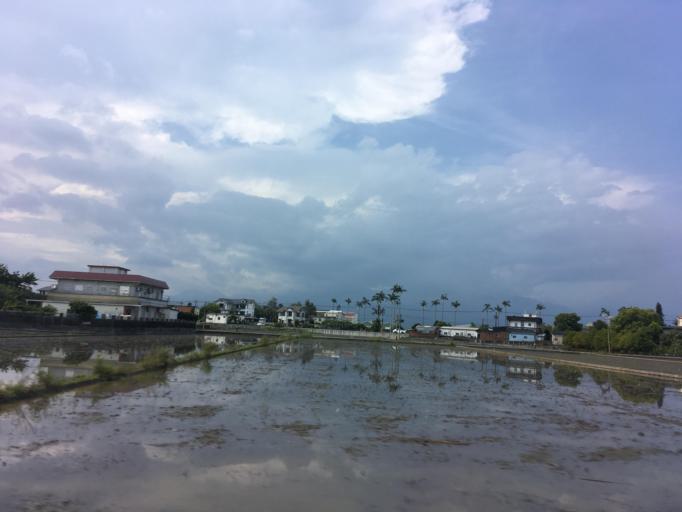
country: TW
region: Taiwan
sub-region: Yilan
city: Yilan
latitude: 24.6926
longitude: 121.7859
